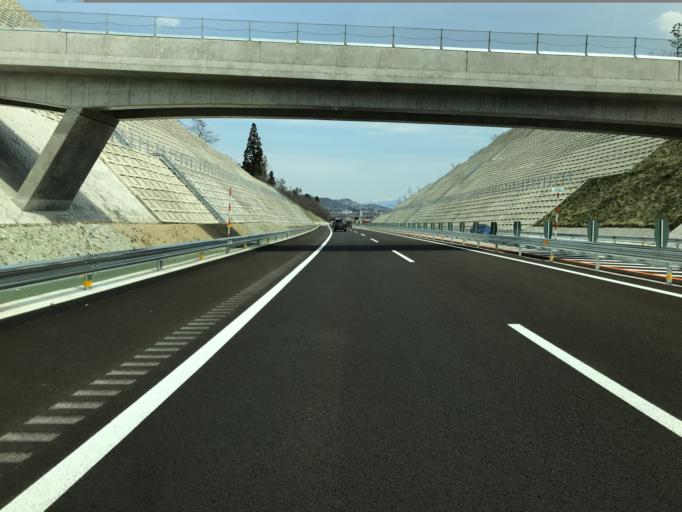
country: JP
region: Yamagata
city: Kaminoyama
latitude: 38.1179
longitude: 140.2482
